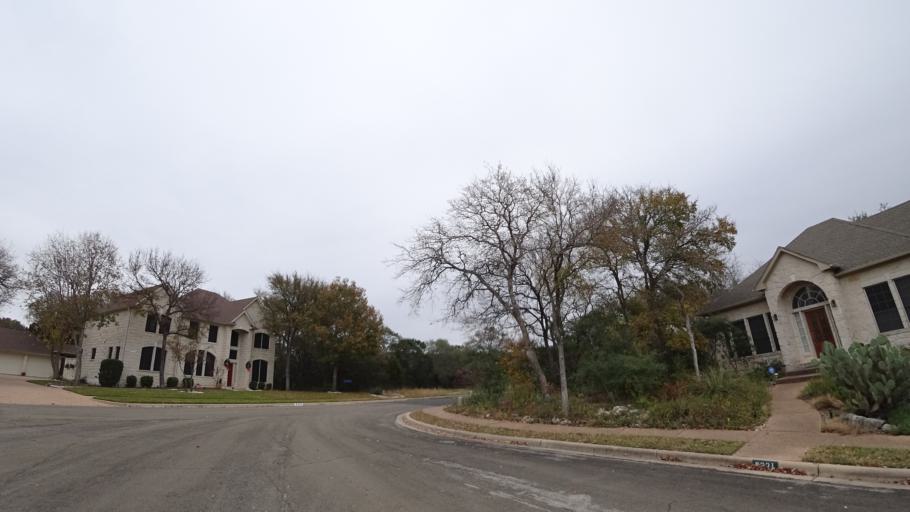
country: US
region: Texas
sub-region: Williamson County
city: Jollyville
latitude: 30.3932
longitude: -97.8039
